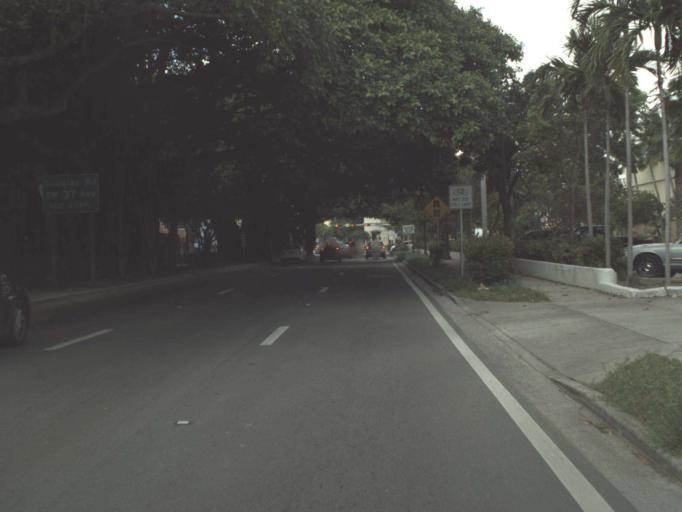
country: US
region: Florida
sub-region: Miami-Dade County
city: Coral Gables
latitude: 25.7500
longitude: -80.2524
